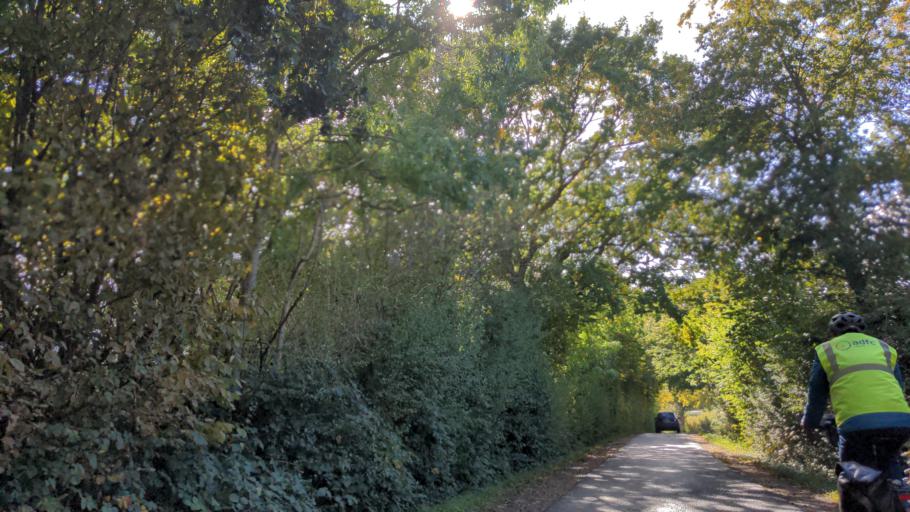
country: DE
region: Schleswig-Holstein
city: Heidekamp
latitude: 53.8326
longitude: 10.5137
